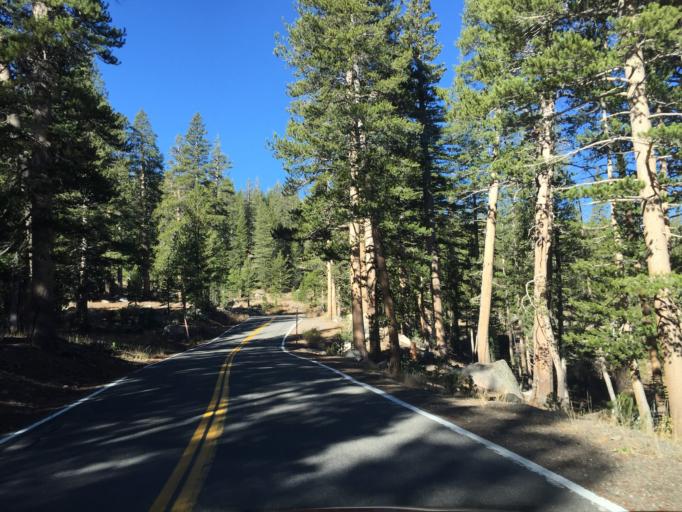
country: US
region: California
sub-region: Mono County
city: Bridgeport
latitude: 38.3106
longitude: -119.5970
